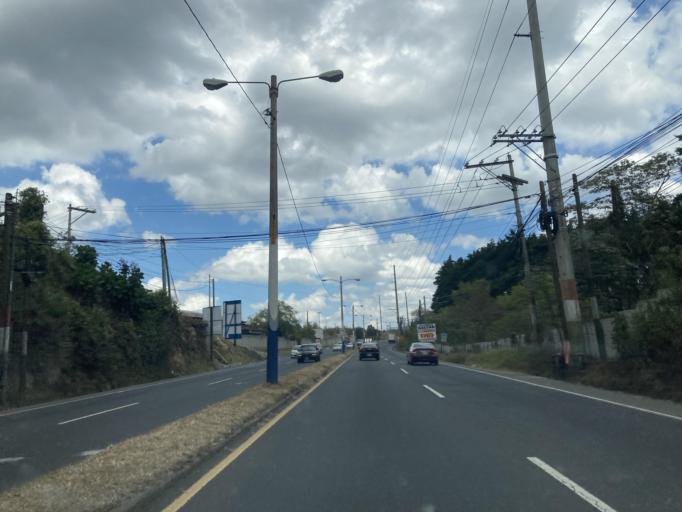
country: GT
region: Guatemala
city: Fraijanes
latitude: 14.5062
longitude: -90.4800
